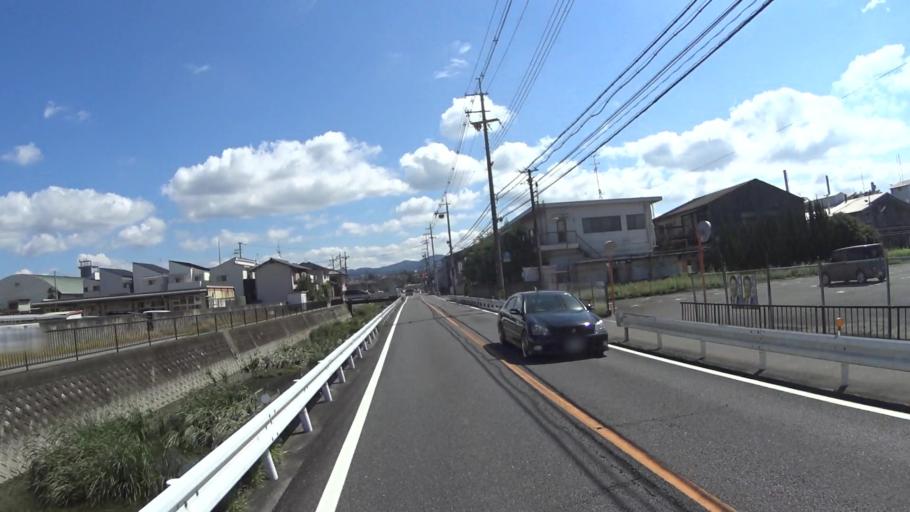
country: JP
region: Kyoto
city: Uji
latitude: 34.8871
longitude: 135.7719
